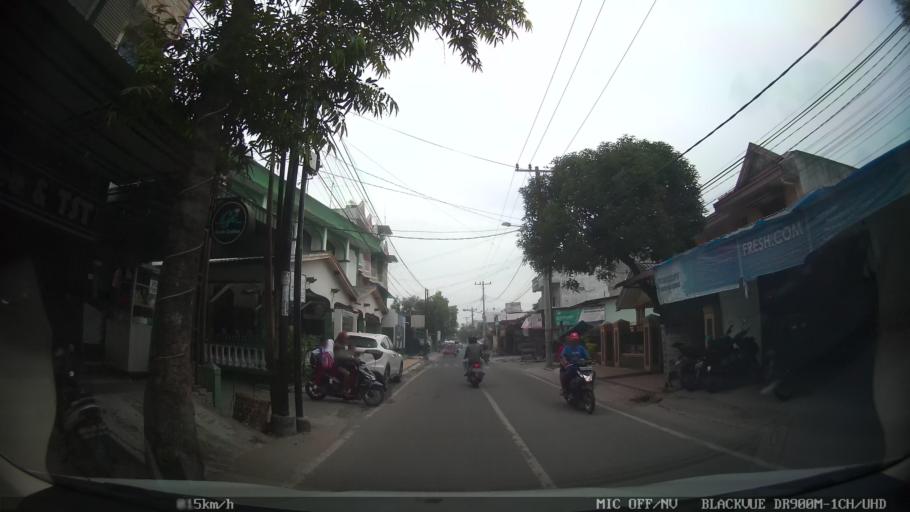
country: ID
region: North Sumatra
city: Medan
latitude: 3.5782
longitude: 98.7020
